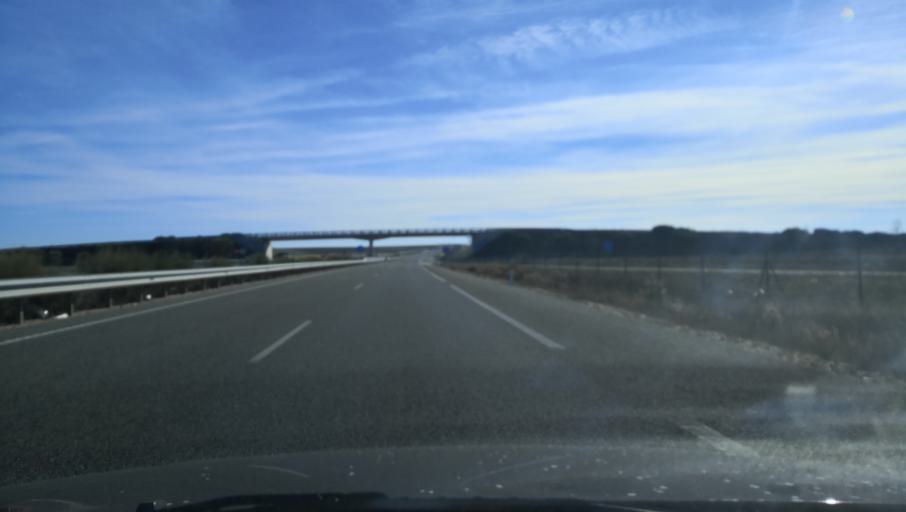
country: ES
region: Castille and Leon
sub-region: Provincia de Salamanca
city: Cantaracillo
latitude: 40.8884
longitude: -5.1501
